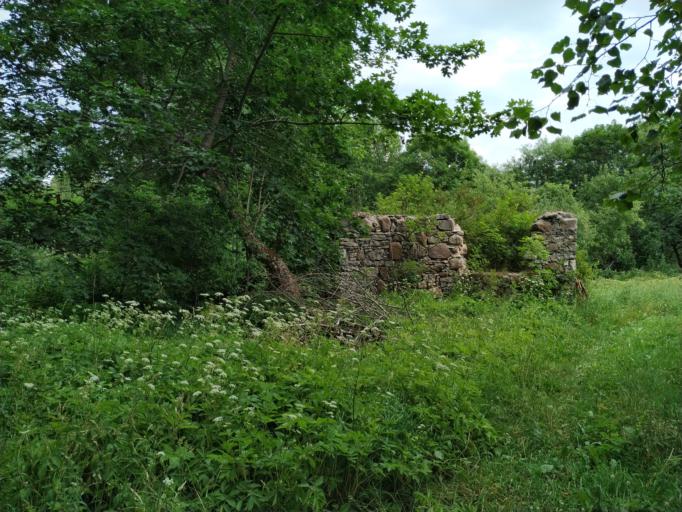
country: LT
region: Panevezys
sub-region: Birzai
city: Birzai
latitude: 56.3594
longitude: 24.9687
